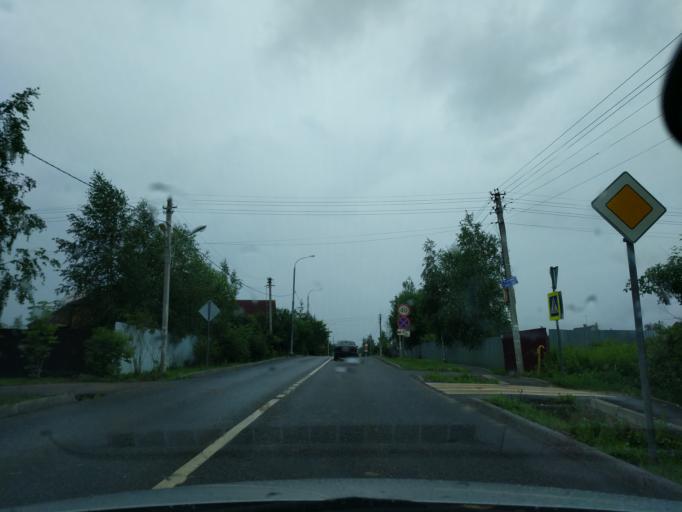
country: RU
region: Moskovskaya
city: Selyatino
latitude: 55.5075
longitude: 36.9345
